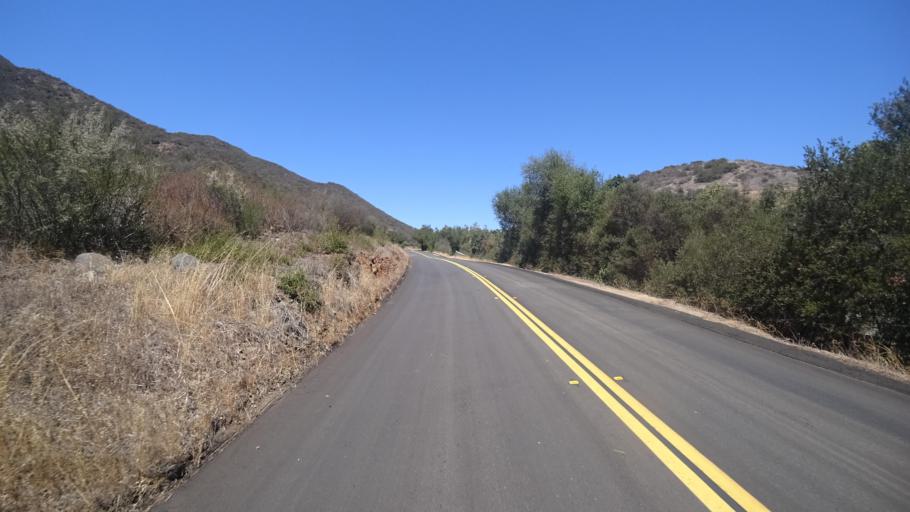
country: US
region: California
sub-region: San Diego County
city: Rainbow
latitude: 33.3651
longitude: -117.1383
